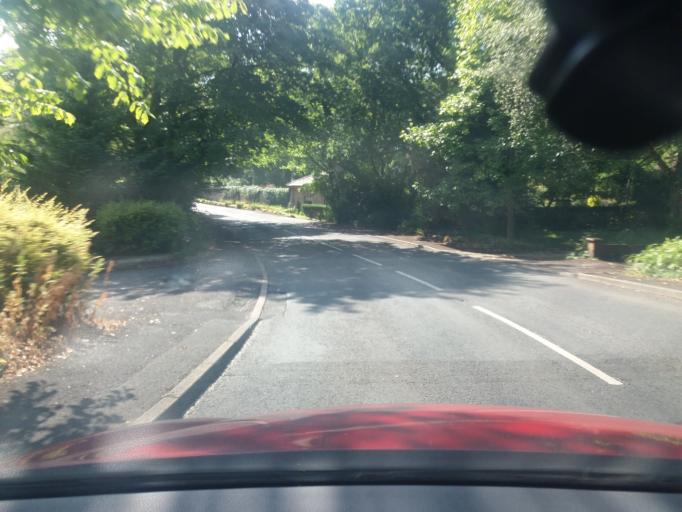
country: GB
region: England
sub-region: Lancashire
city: Adlington
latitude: 53.6229
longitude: -2.6145
